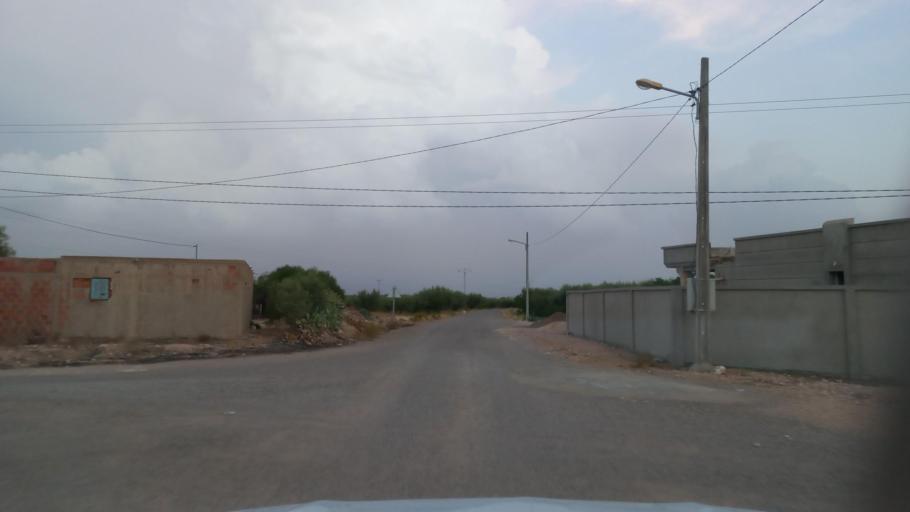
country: TN
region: Al Qasrayn
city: Kasserine
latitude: 35.2734
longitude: 9.0364
